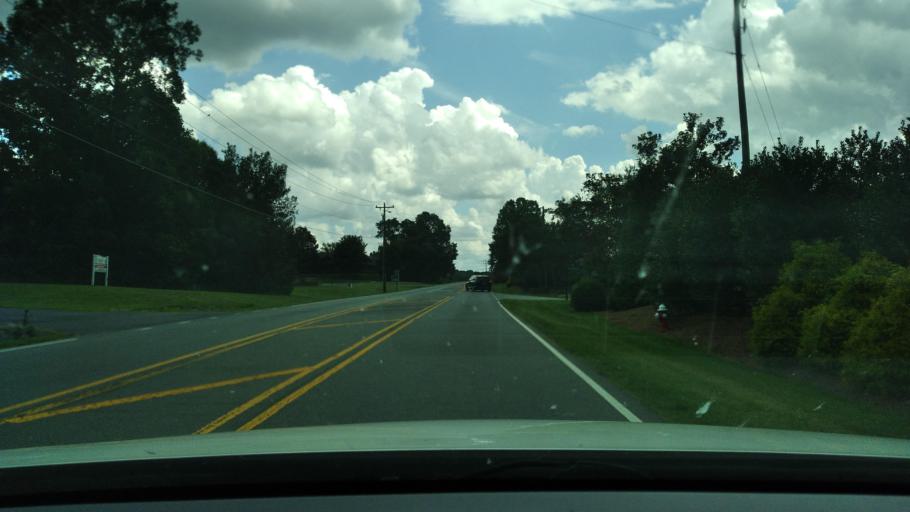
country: US
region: North Carolina
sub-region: Alamance County
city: Elon
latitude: 36.0849
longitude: -79.5173
